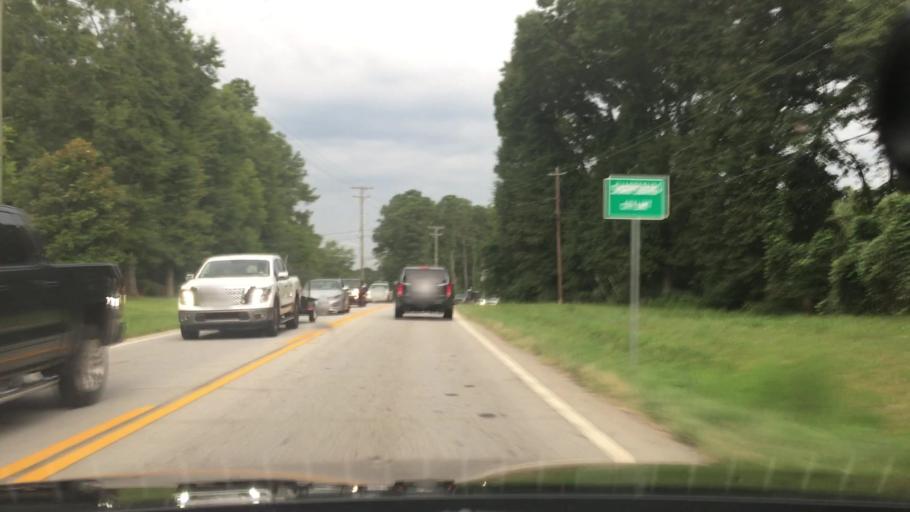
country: US
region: Georgia
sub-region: Fayette County
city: Peachtree City
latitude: 33.3352
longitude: -84.6471
